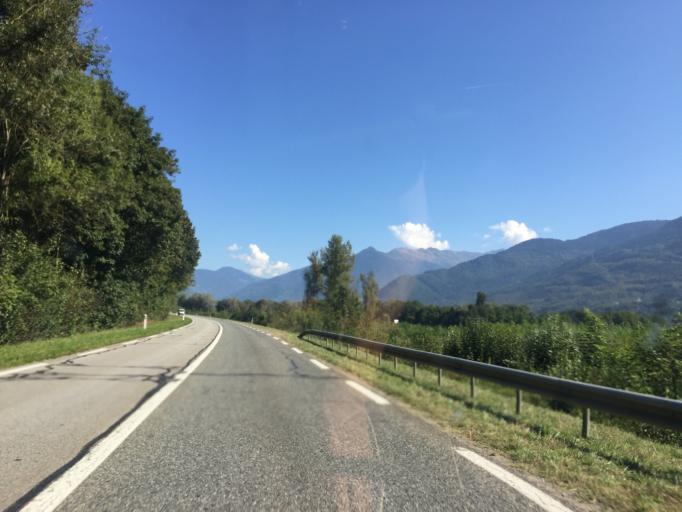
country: FR
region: Rhone-Alpes
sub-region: Departement de la Savoie
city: Frontenex
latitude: 45.6289
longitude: 6.3251
